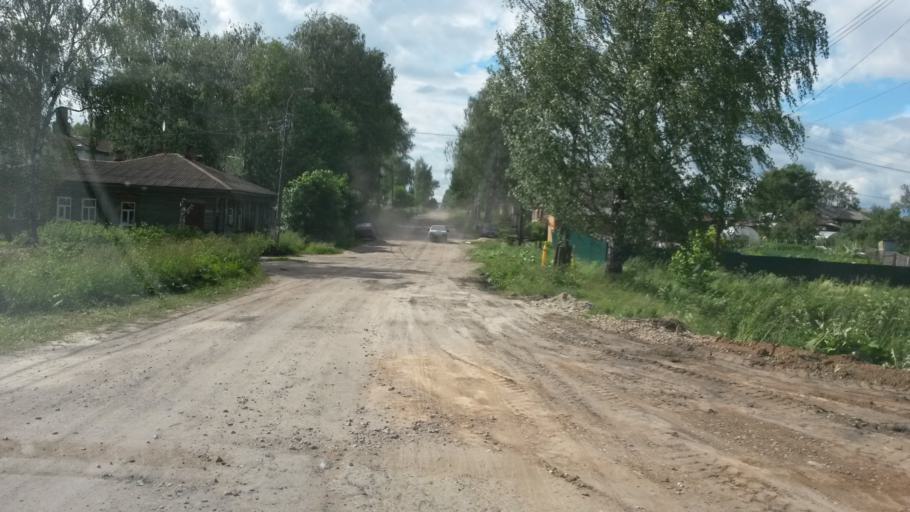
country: RU
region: Jaroslavl
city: Tutayev
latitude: 57.8860
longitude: 39.5385
